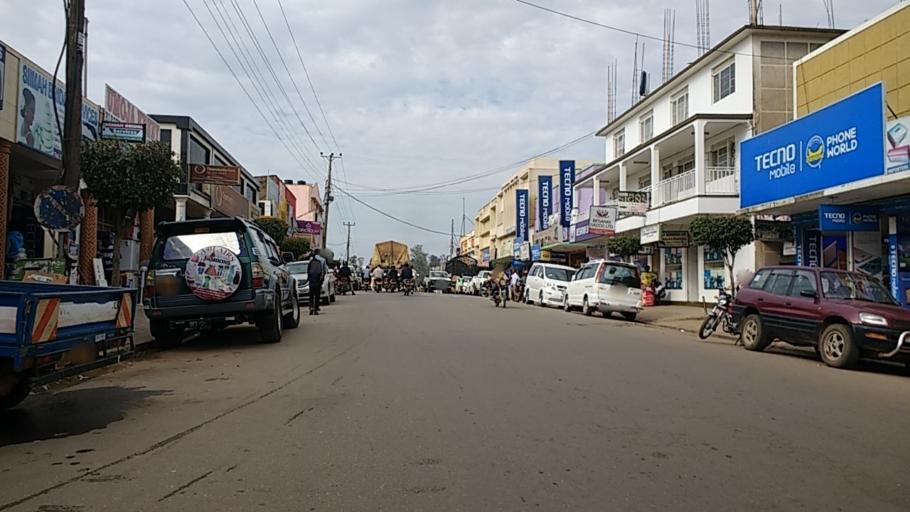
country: UG
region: Western Region
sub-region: Mbarara District
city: Mbarara
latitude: -0.6059
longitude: 30.6620
